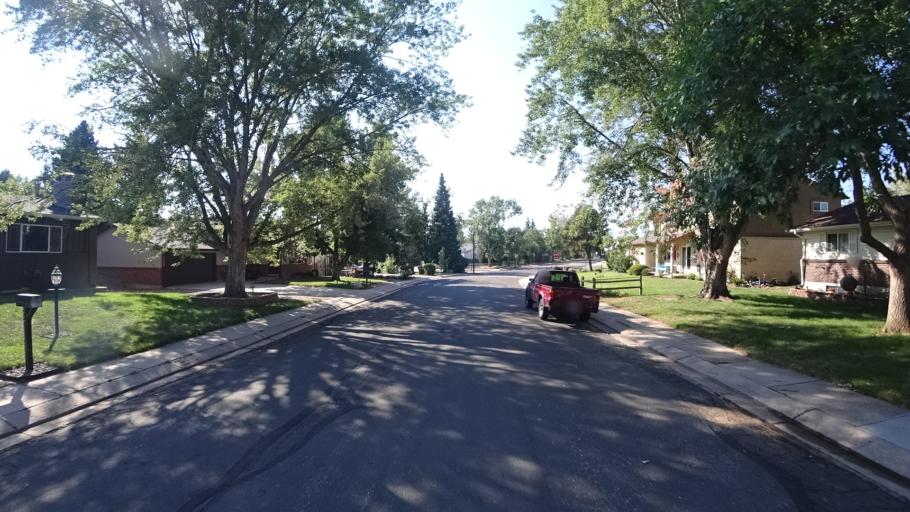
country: US
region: Colorado
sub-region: El Paso County
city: Colorado Springs
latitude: 38.8937
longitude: -104.8387
